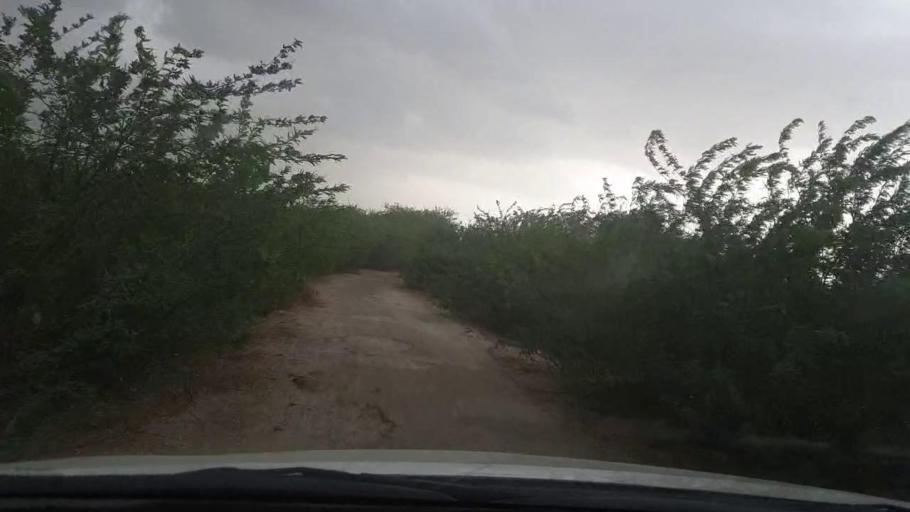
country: PK
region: Sindh
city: Khairpur
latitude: 27.4430
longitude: 68.9871
